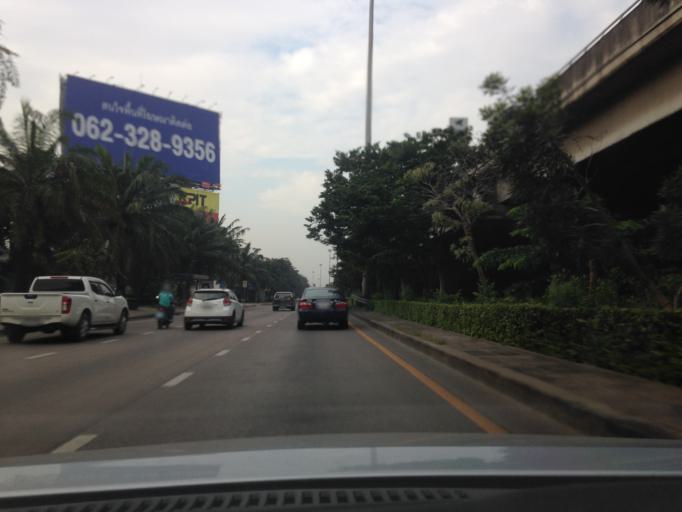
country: TH
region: Bangkok
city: Lat Phrao
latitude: 13.8152
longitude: 100.6229
